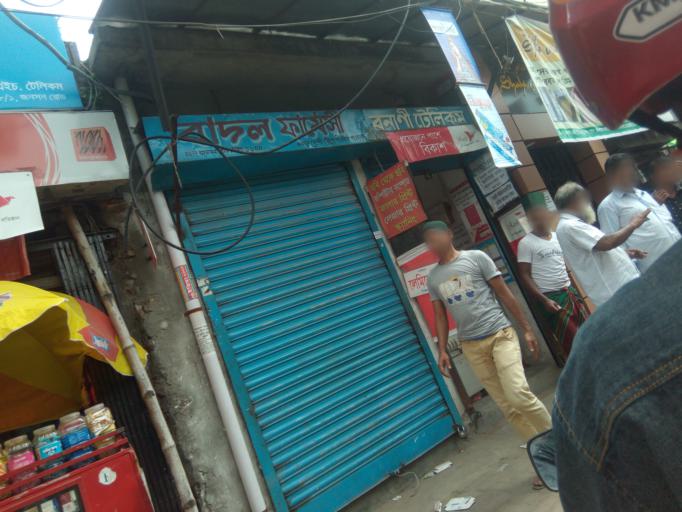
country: BD
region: Dhaka
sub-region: Dhaka
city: Dhaka
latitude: 23.7124
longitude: 90.4113
